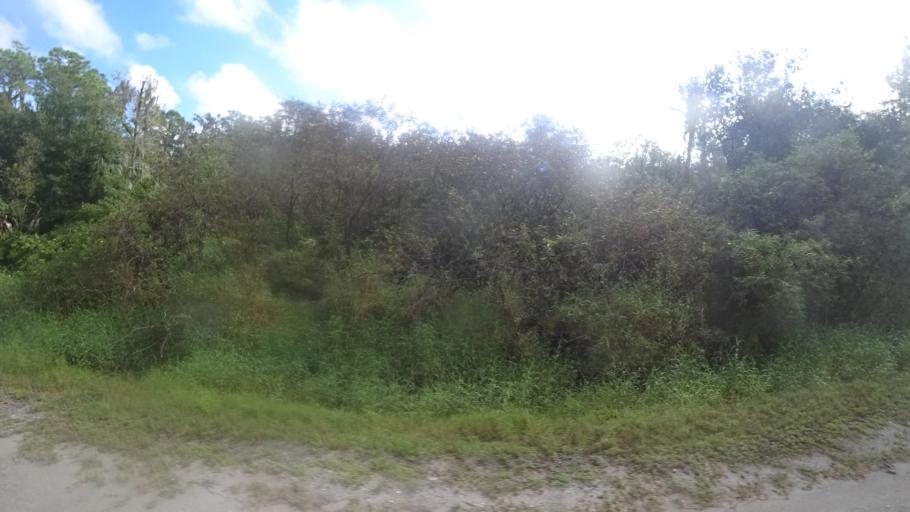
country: US
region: Florida
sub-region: Hillsborough County
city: Sun City Center
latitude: 27.6004
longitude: -82.3638
